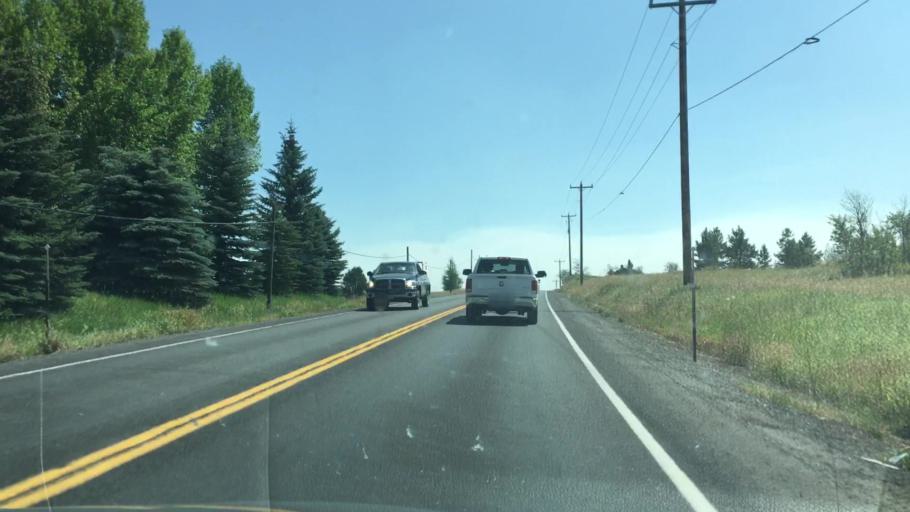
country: US
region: Idaho
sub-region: Valley County
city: McCall
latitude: 44.8821
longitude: -116.0907
